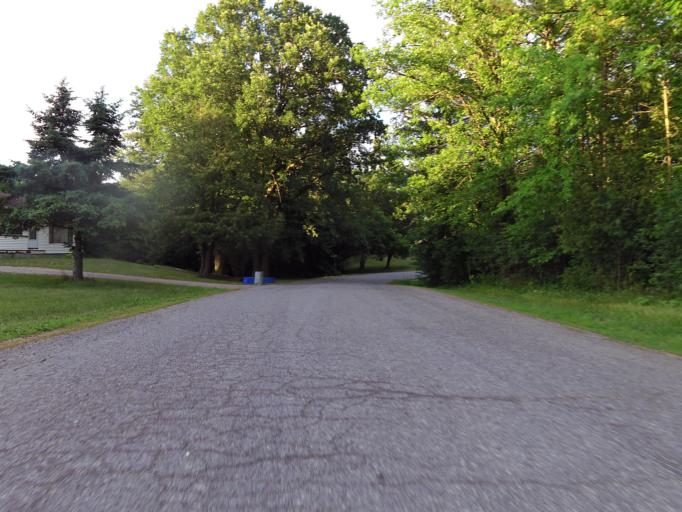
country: CA
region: Ontario
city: Arnprior
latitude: 45.3348
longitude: -76.2933
